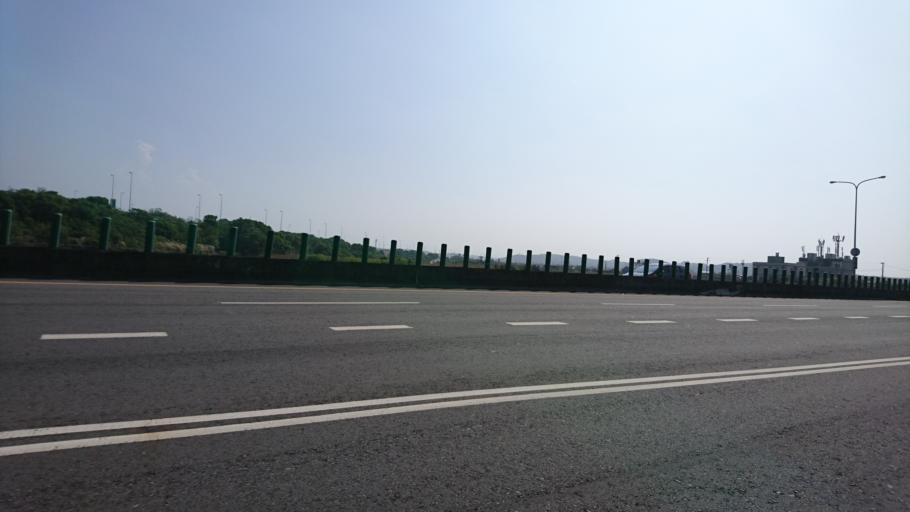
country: TW
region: Taiwan
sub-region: Miaoli
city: Miaoli
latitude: 24.6798
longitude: 120.8456
